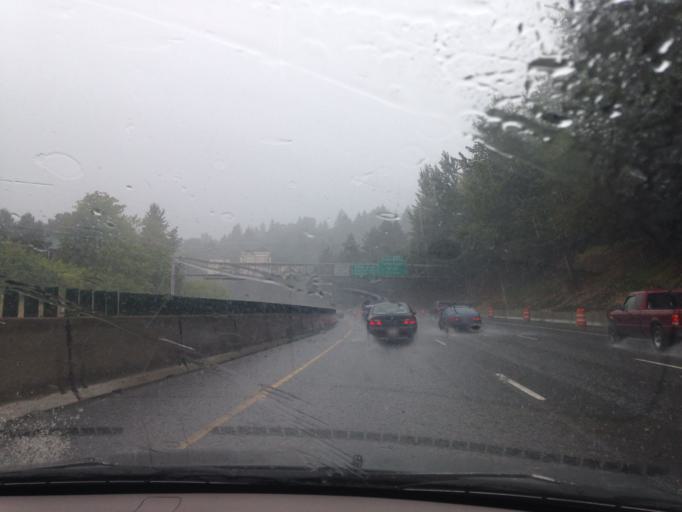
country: US
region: Oregon
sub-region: Multnomah County
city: Portland
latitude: 45.4881
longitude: -122.6778
